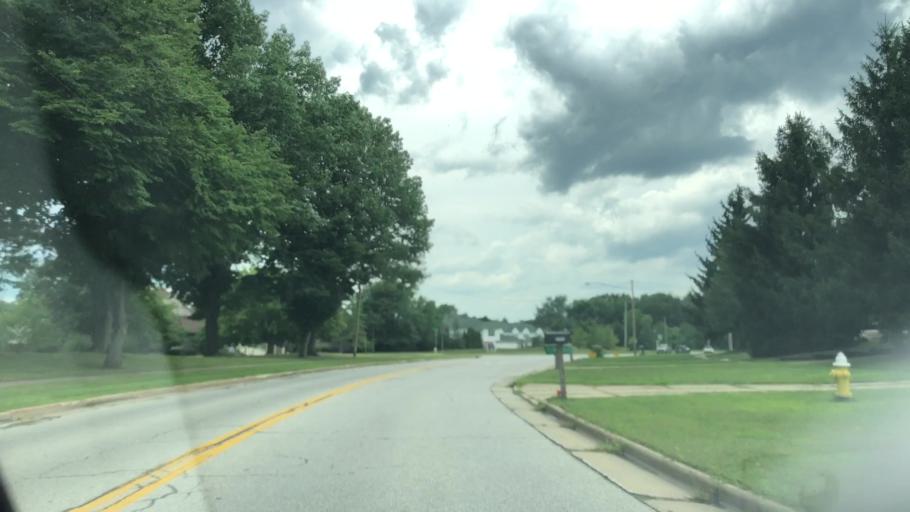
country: US
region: Ohio
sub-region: Summit County
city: Fairlawn
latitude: 41.1321
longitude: -81.6085
